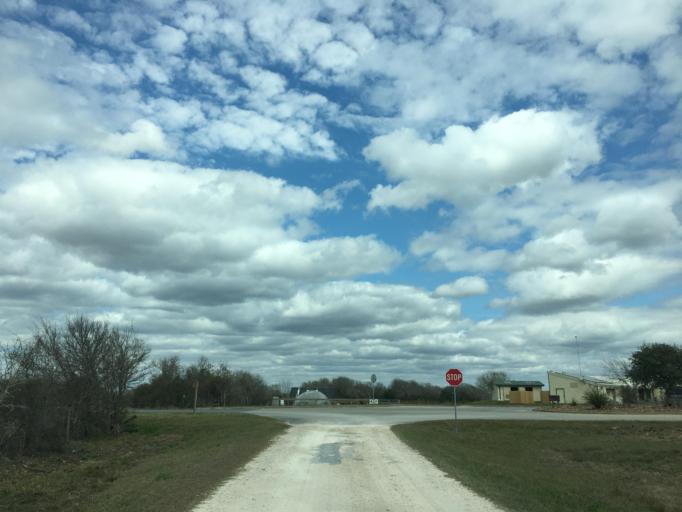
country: US
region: Texas
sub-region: Brazoria County
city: Oyster Creek
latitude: 29.0591
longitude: -95.2688
